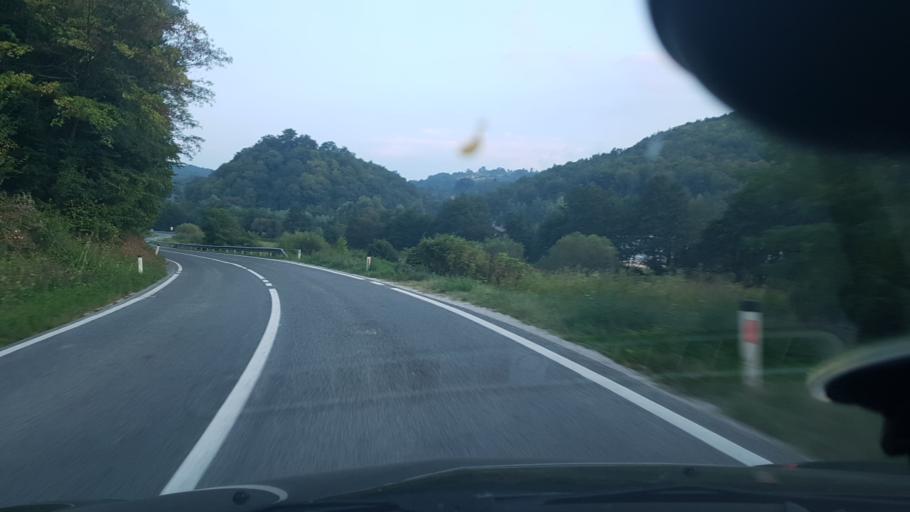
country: SI
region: Rogatec
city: Rogatec
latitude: 46.2196
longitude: 15.7279
